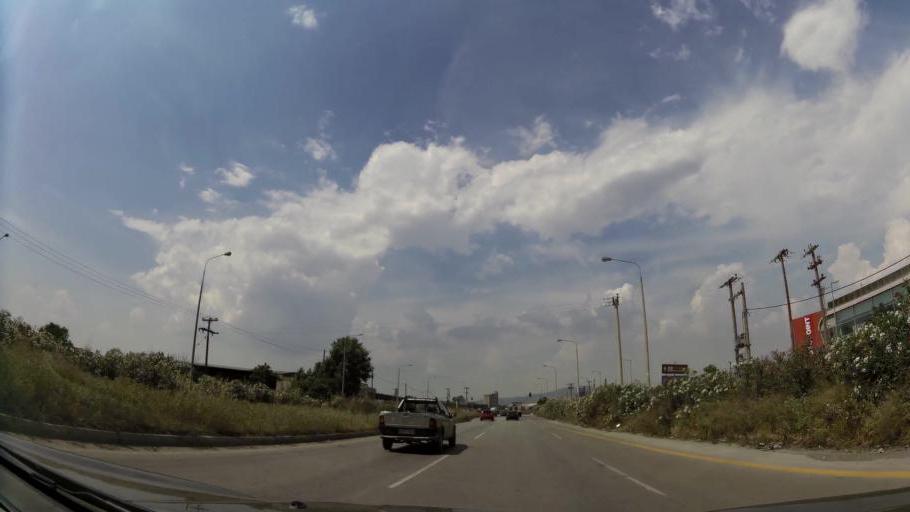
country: GR
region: Central Macedonia
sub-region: Nomos Thessalonikis
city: Menemeni
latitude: 40.6621
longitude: 22.8818
